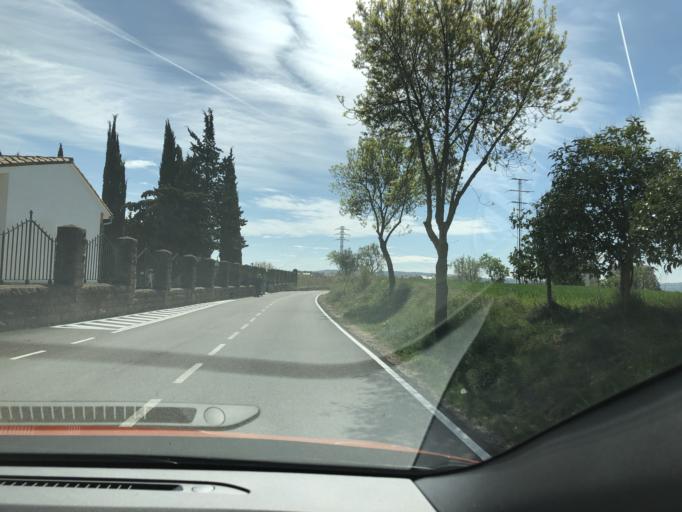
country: ES
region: Catalonia
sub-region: Provincia de Lleida
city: Solsona
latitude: 41.9992
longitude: 1.5243
